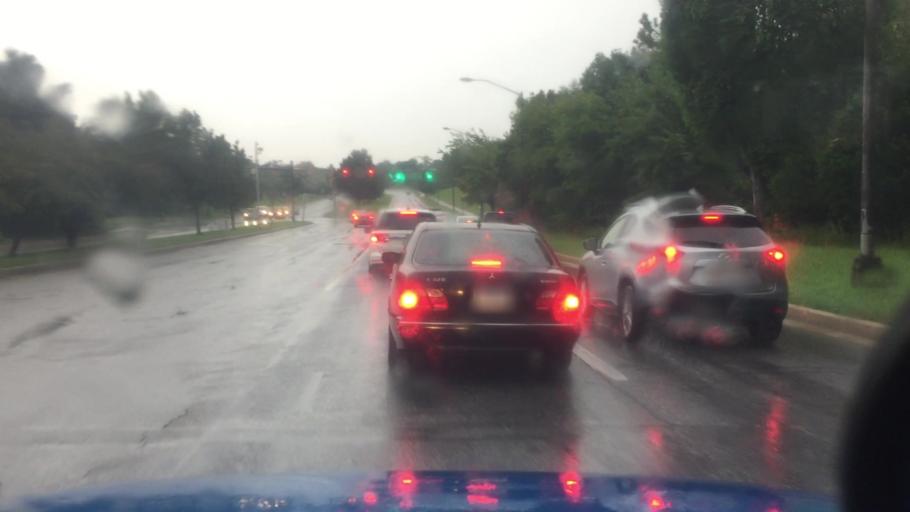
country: US
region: Maryland
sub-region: Howard County
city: Columbia
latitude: 39.1948
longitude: -76.8091
